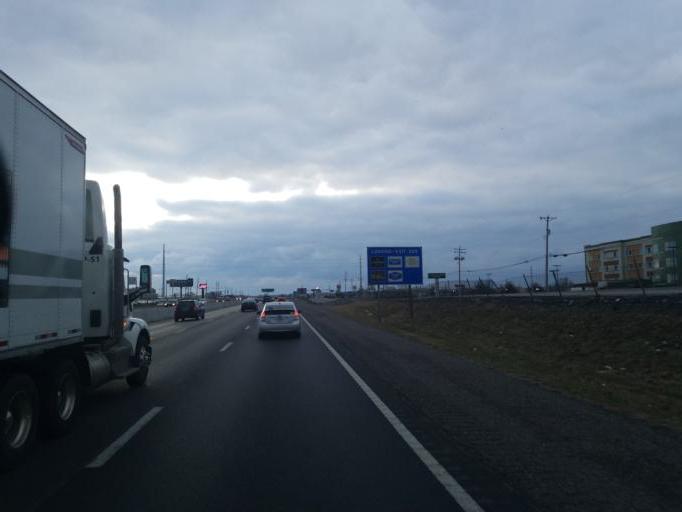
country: US
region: Missouri
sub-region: Saint Charles County
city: Saint Peters
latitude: 38.7971
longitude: -90.5800
